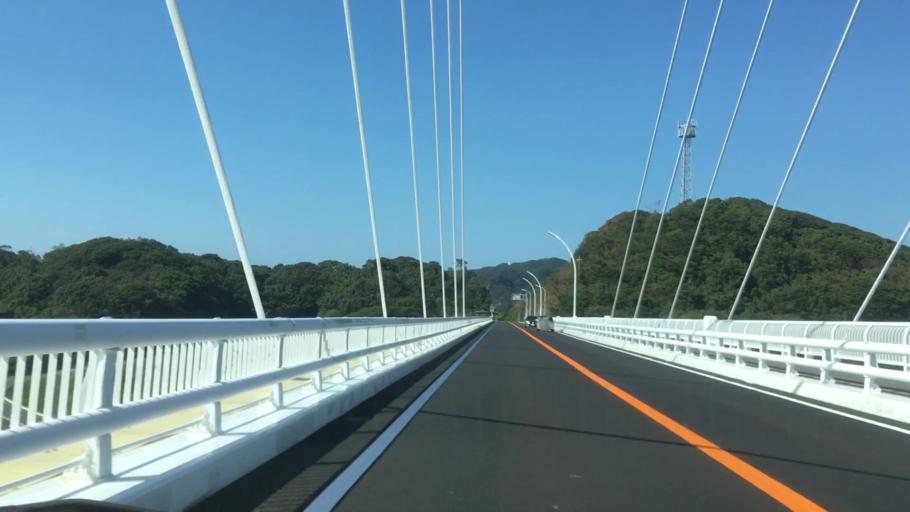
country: JP
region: Nagasaki
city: Sasebo
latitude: 33.0377
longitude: 129.6392
